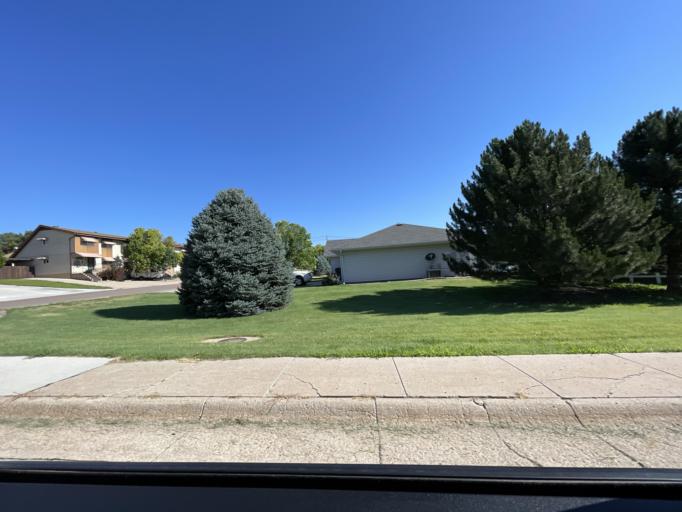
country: US
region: Nebraska
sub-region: Red Willow County
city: McCook
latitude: 40.2046
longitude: -100.6159
